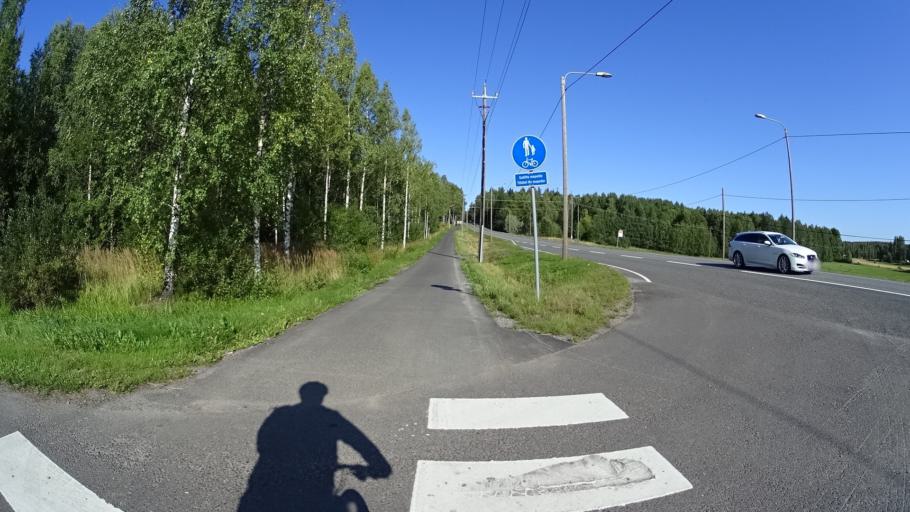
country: FI
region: Uusimaa
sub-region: Helsinki
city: Kilo
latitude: 60.2909
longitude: 24.7823
